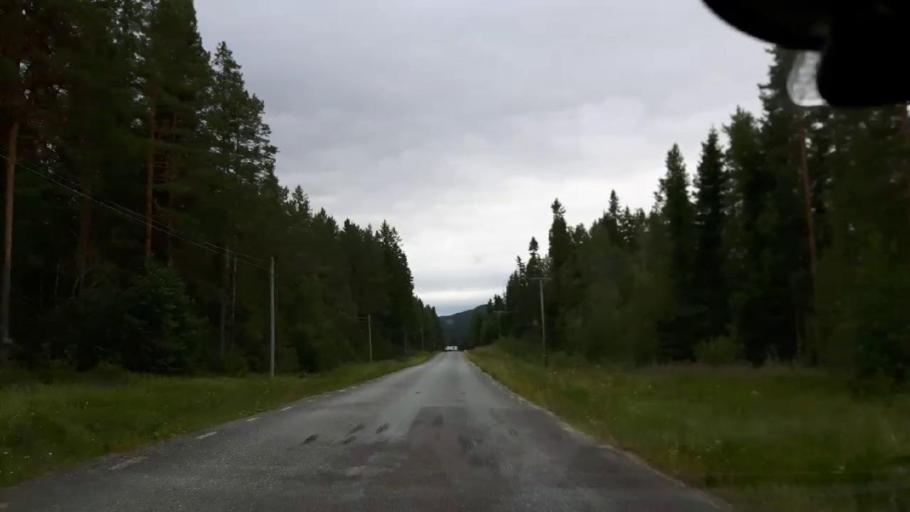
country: SE
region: Jaemtland
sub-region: Braecke Kommun
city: Braecke
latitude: 62.8752
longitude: 15.6172
